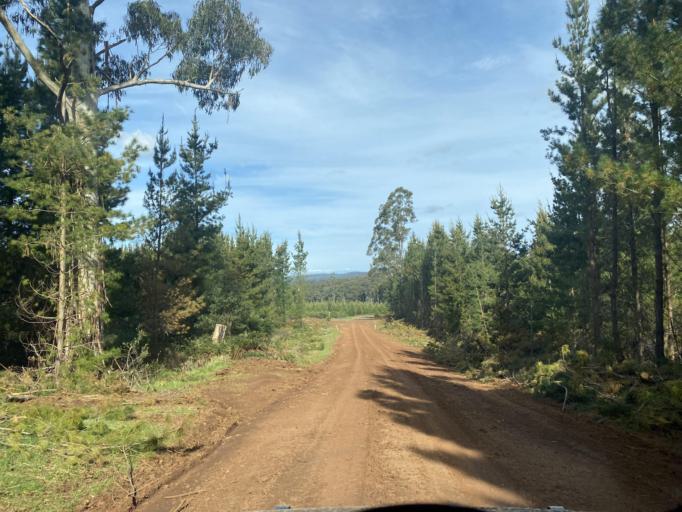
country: AU
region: Victoria
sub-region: Mansfield
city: Mansfield
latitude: -36.8384
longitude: 146.1802
